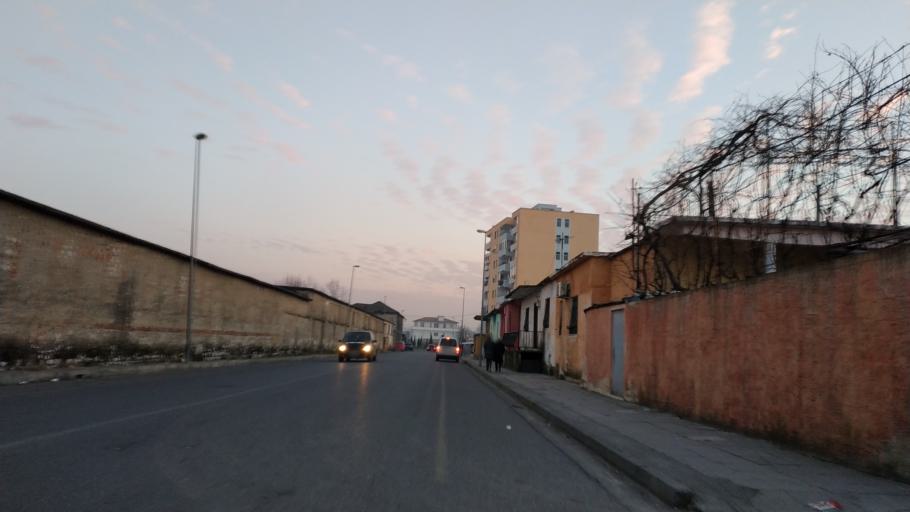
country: AL
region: Shkoder
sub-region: Rrethi i Shkodres
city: Shkoder
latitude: 42.0769
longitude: 19.5236
